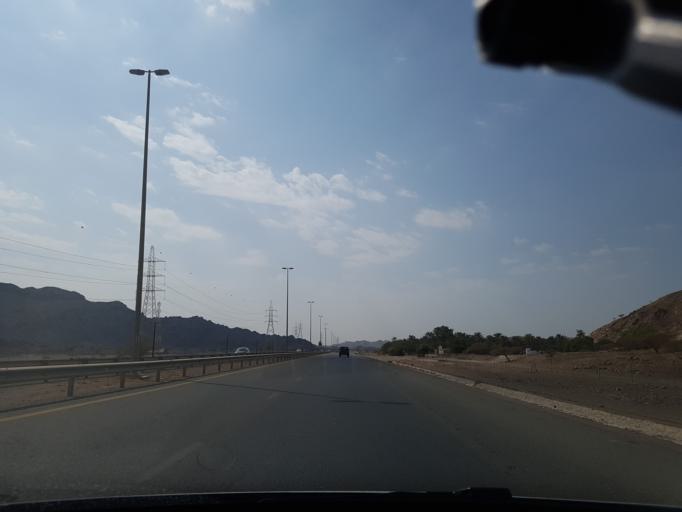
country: AE
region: Al Fujayrah
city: Dibba Al-Fujairah
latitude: 25.4918
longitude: 56.0515
